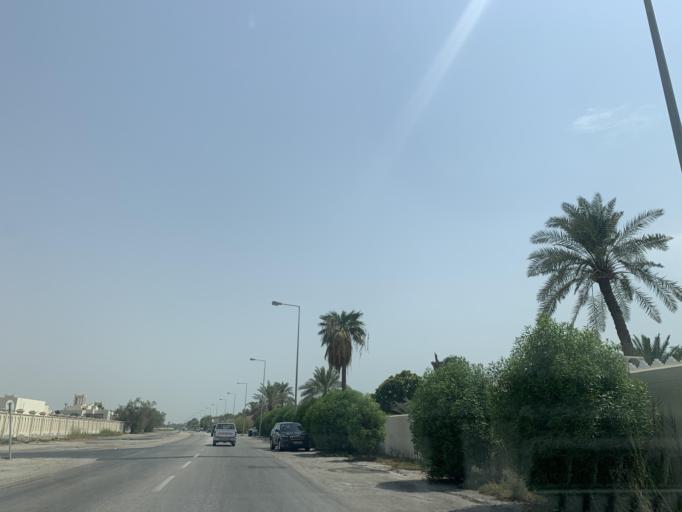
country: BH
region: Central Governorate
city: Madinat Hamad
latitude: 26.1644
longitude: 50.4653
